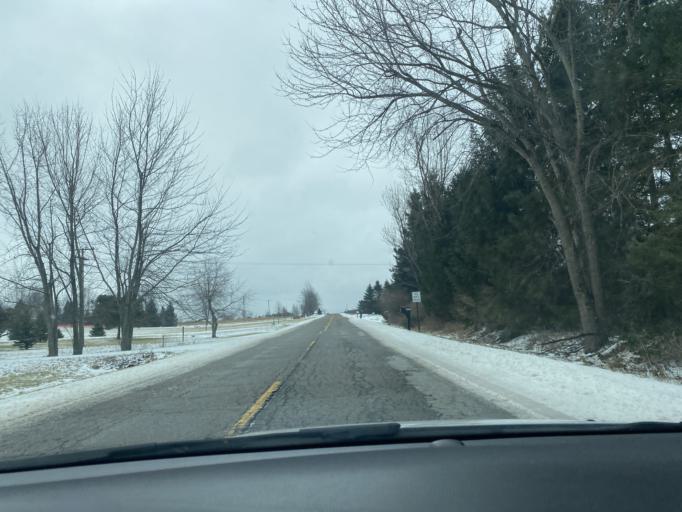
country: US
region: Michigan
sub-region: Lapeer County
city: North Branch
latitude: 43.2088
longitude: -83.1489
